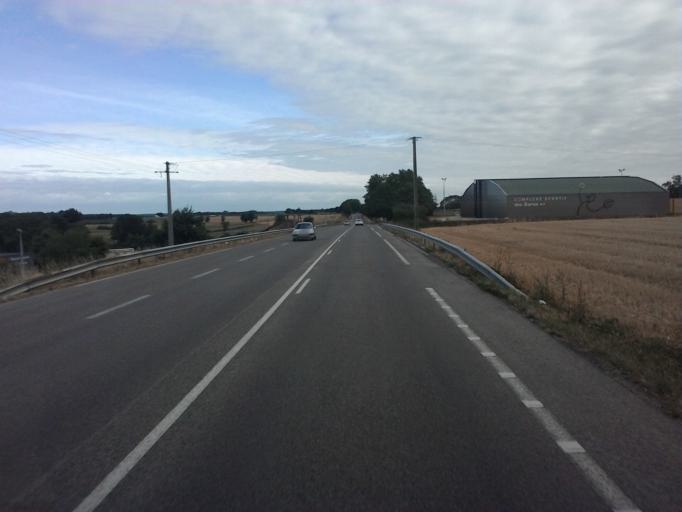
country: FR
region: Rhone-Alpes
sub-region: Departement de l'Ain
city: Saint-Martin-du-Mont
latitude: 46.0942
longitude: 5.3128
